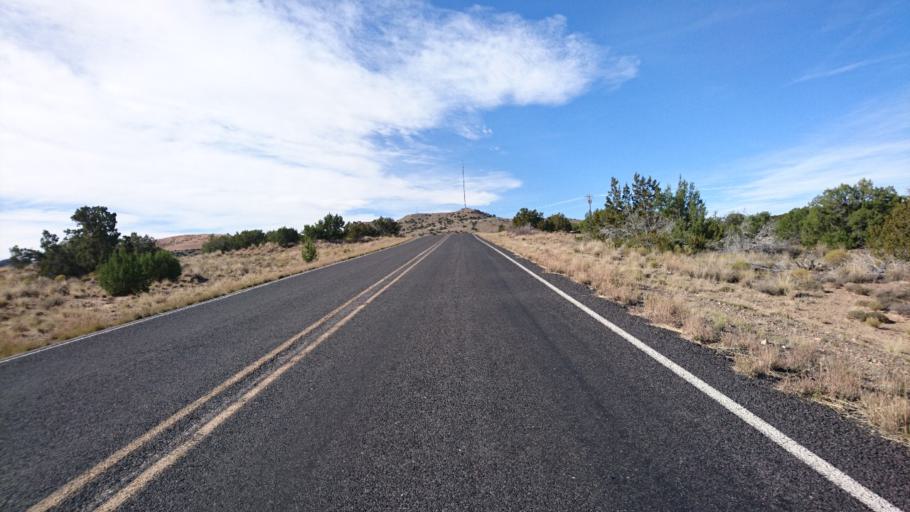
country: US
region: New Mexico
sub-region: Cibola County
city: Laguna
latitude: 35.0434
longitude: -107.3520
